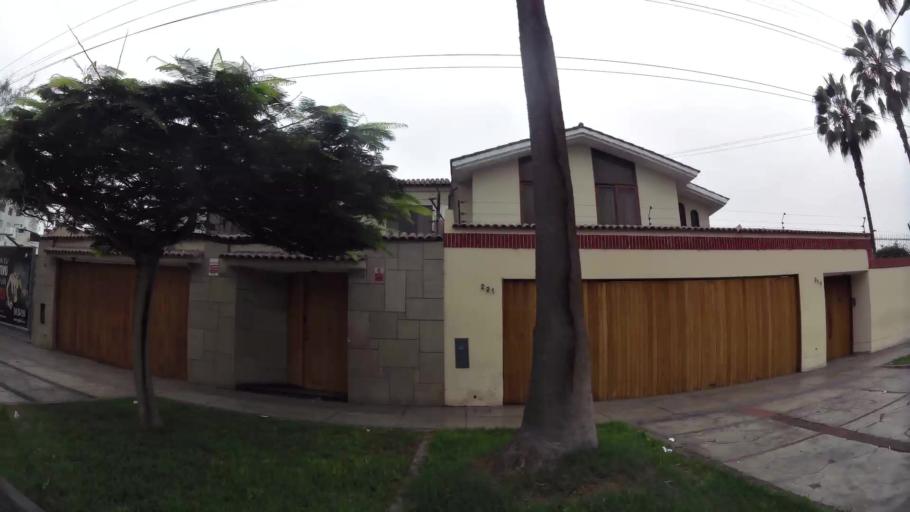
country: PE
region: Lima
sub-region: Lima
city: San Luis
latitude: -12.0933
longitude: -77.0062
